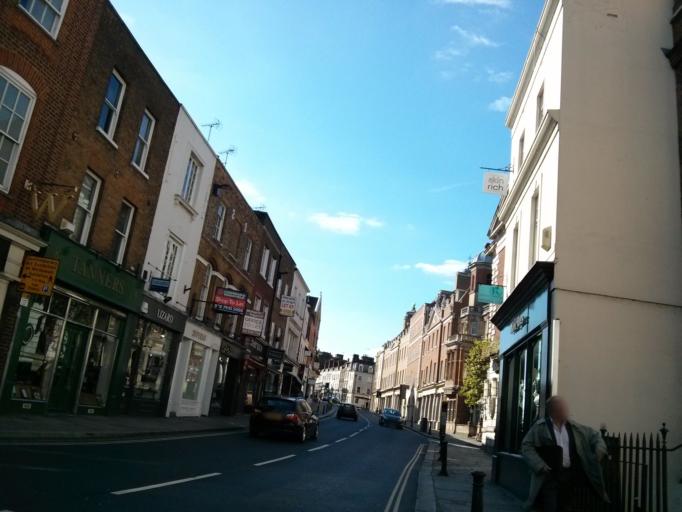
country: GB
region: England
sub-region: Greater London
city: Richmond
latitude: 51.4594
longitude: -0.3063
